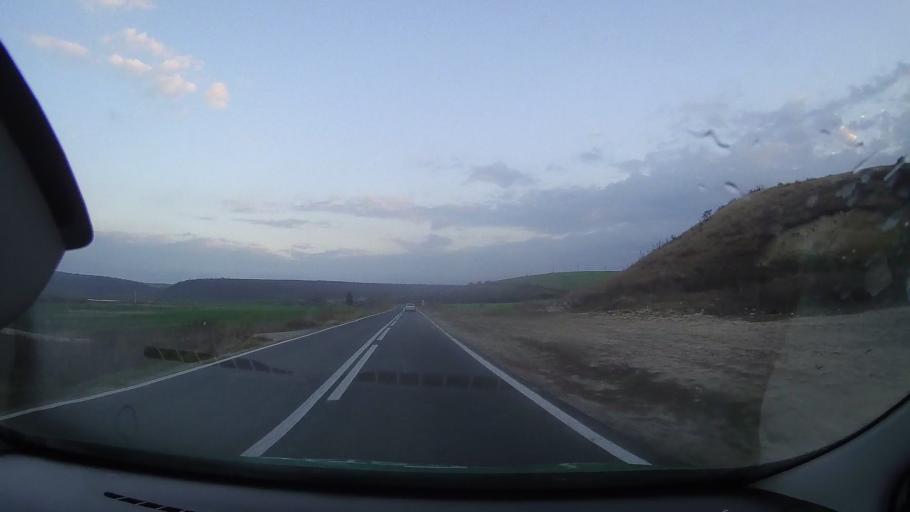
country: RO
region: Constanta
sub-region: Comuna Lipnita
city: Lipnita
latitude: 44.0993
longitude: 27.6292
